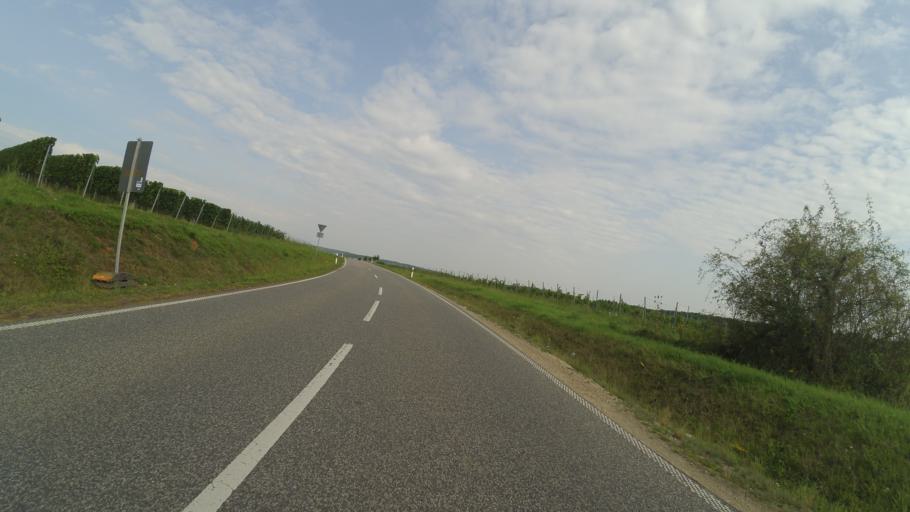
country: LU
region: Grevenmacher
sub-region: Canton de Grevenmacher
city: Wormeldange
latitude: 49.5836
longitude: 6.3940
